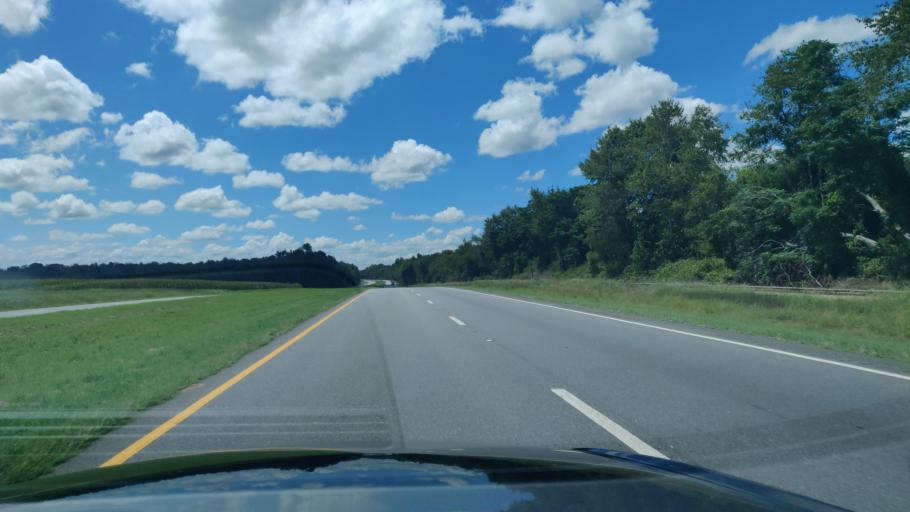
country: US
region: Georgia
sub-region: Terrell County
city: Dawson
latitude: 31.7297
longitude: -84.3633
